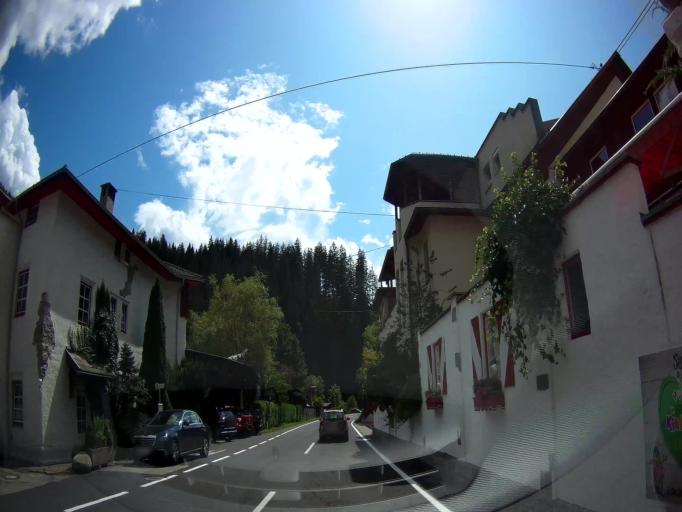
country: AT
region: Carinthia
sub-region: Politischer Bezirk Spittal an der Drau
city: Trebesing
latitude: 46.8660
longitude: 13.5065
